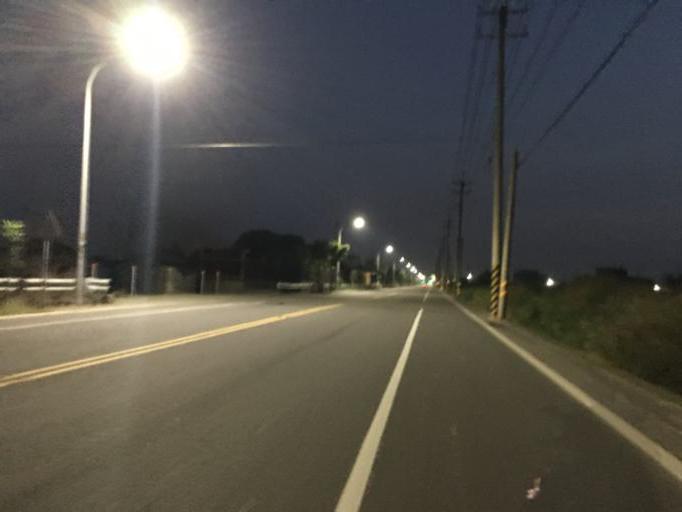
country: TW
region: Taiwan
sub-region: Chiayi
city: Taibao
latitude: 23.5209
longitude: 120.3192
